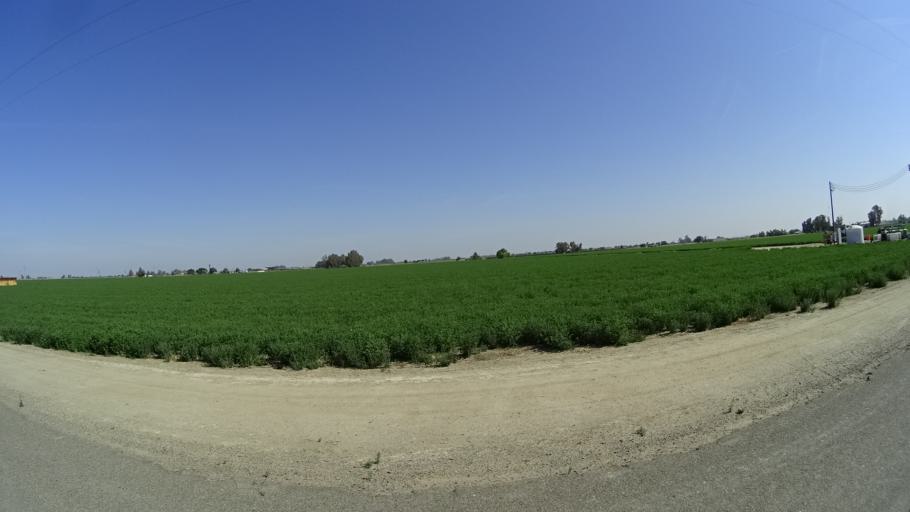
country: US
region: California
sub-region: Fresno County
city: Riverdale
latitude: 36.3511
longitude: -119.8745
